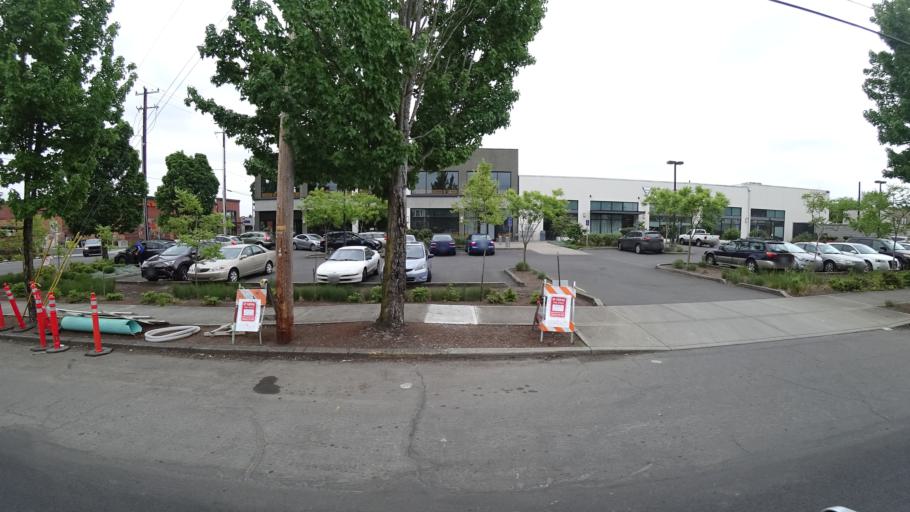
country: US
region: Oregon
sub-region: Multnomah County
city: Portland
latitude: 45.5588
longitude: -122.6626
